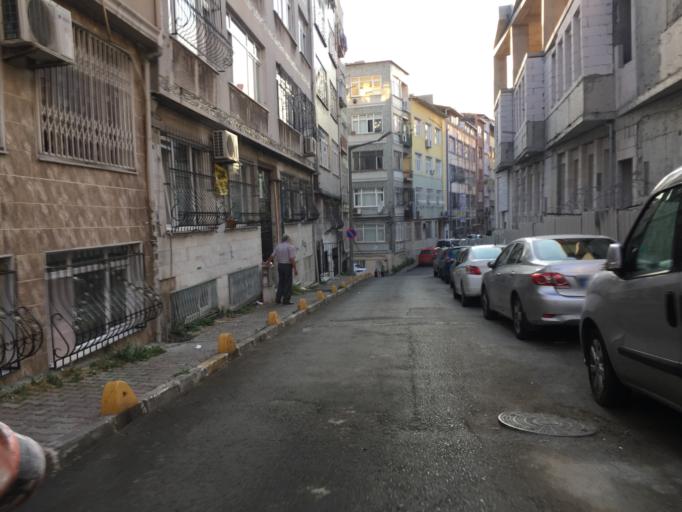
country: TR
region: Istanbul
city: Istanbul
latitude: 41.0163
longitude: 28.9480
